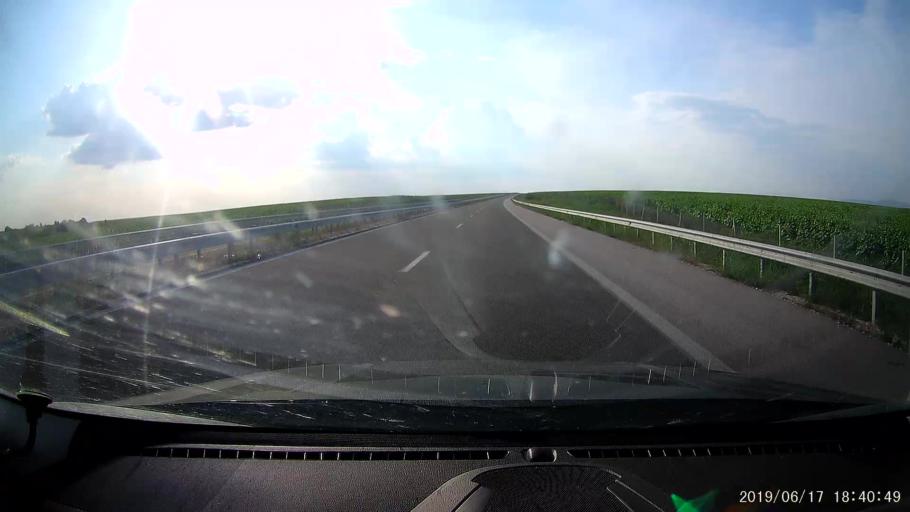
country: BG
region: Stara Zagora
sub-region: Obshtina Chirpan
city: Chirpan
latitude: 42.1611
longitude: 25.2683
